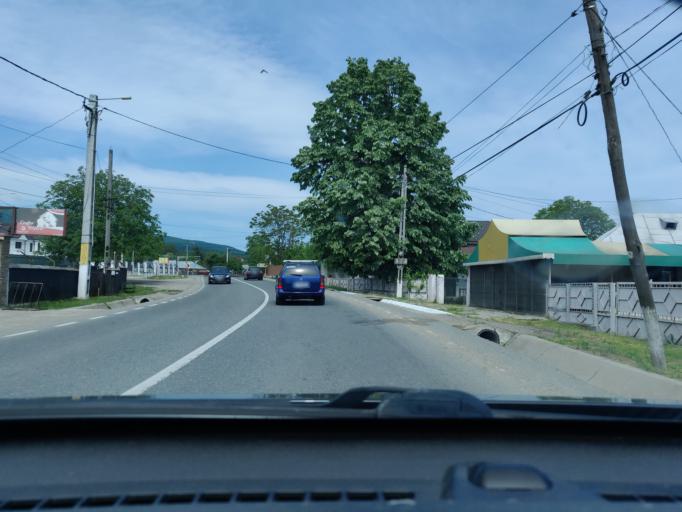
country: RO
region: Vrancea
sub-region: Comuna Bolotesti
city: Gagesti
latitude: 45.8601
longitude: 27.0490
